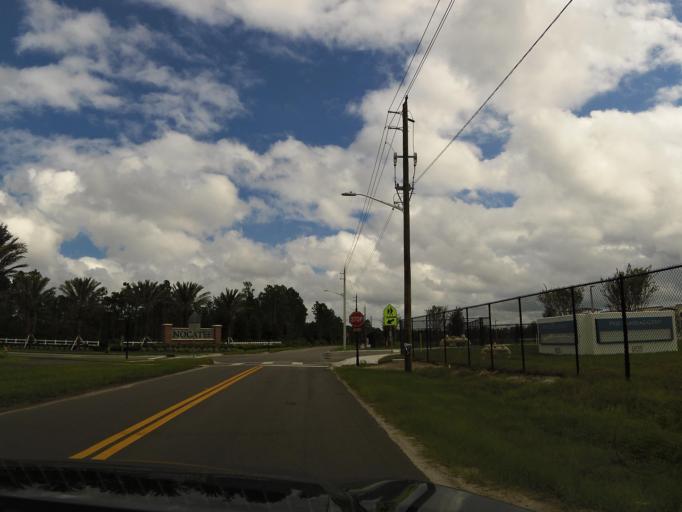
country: US
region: Florida
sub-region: Saint Johns County
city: Palm Valley
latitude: 30.0509
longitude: -81.3963
